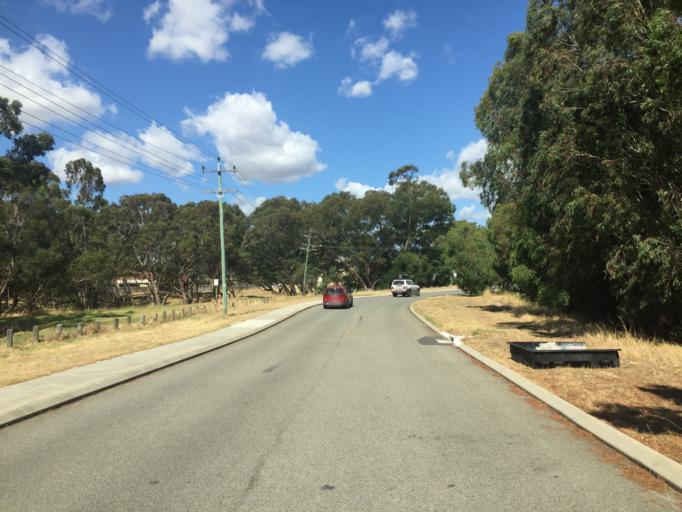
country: AU
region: Western Australia
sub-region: Belmont
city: Redcliffe
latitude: -31.9274
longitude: 115.9440
